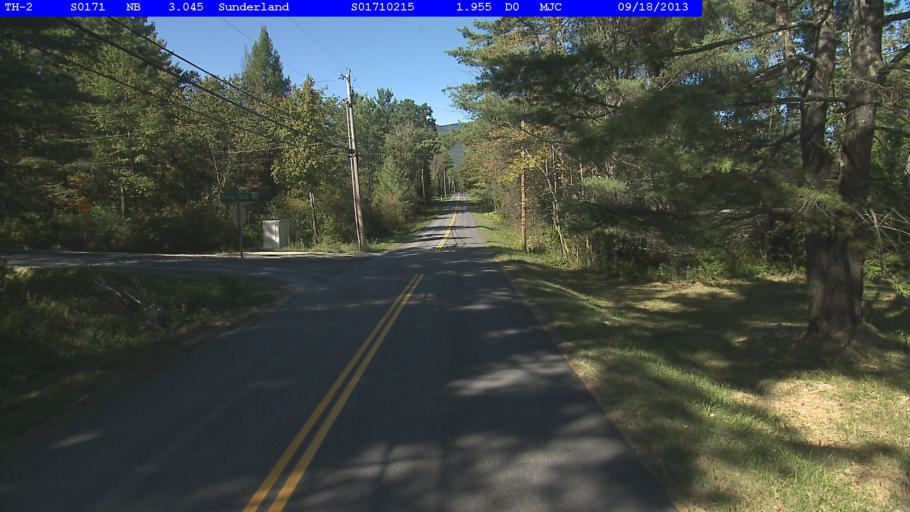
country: US
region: Vermont
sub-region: Bennington County
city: Arlington
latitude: 43.0929
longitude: -73.1237
